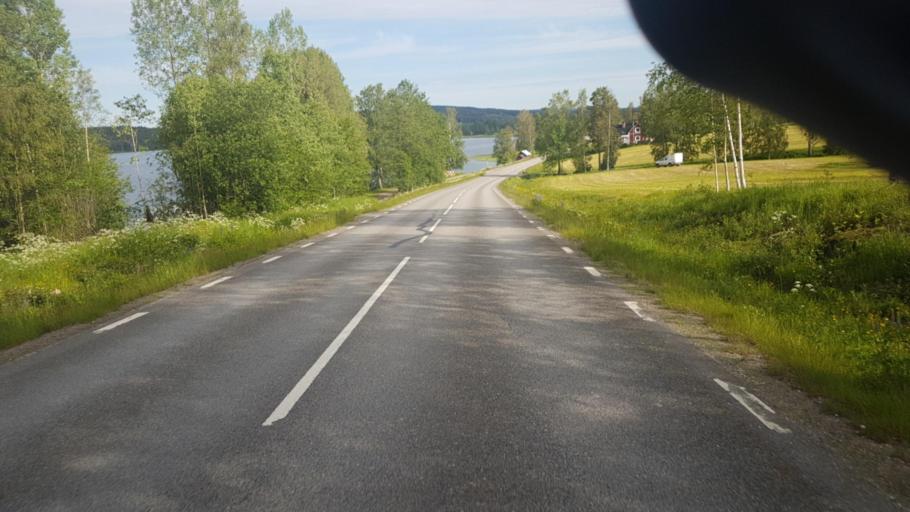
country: SE
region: Vaermland
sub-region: Arvika Kommun
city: Arvika
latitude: 59.7391
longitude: 12.5589
